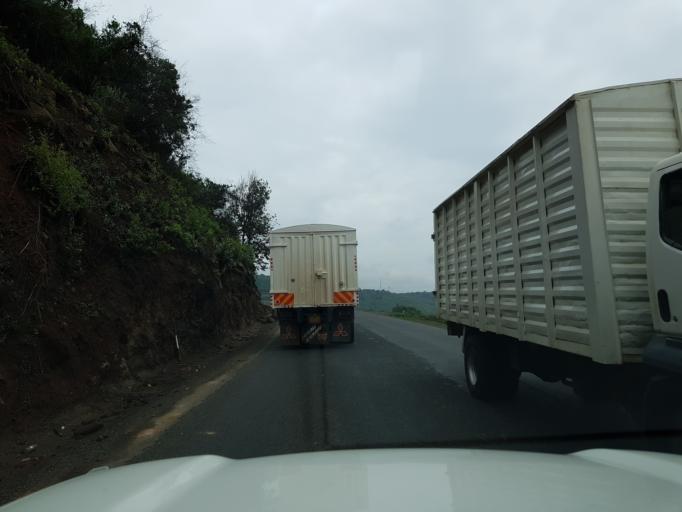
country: KE
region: Kiambu
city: Limuru
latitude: -1.0530
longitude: 36.6017
